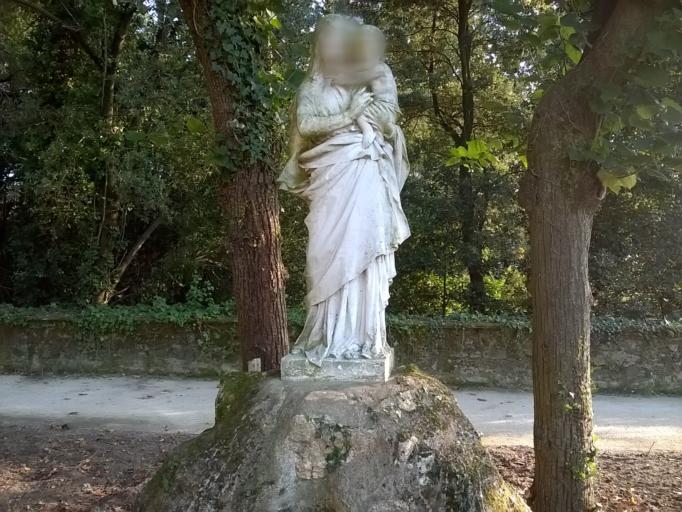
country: FR
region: Pays de la Loire
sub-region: Departement de la Loire-Atlantique
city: Nantes
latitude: 47.1994
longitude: -1.5866
